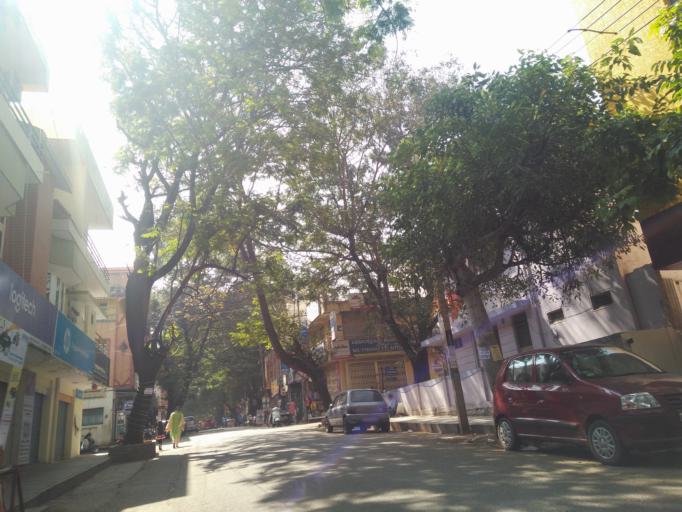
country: IN
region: Karnataka
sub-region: Bangalore Urban
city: Bangalore
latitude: 12.9719
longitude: 77.5439
